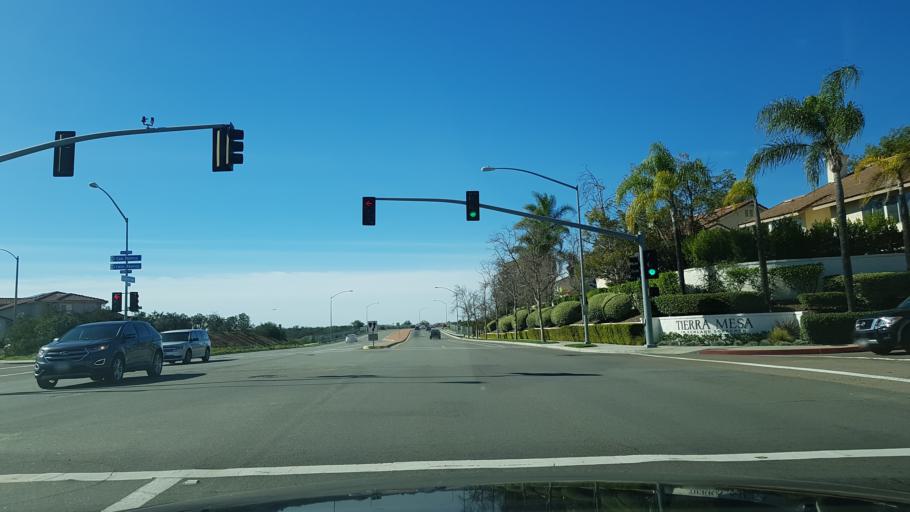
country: US
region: California
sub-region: San Diego County
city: Fairbanks Ranch
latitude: 32.9207
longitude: -117.1697
